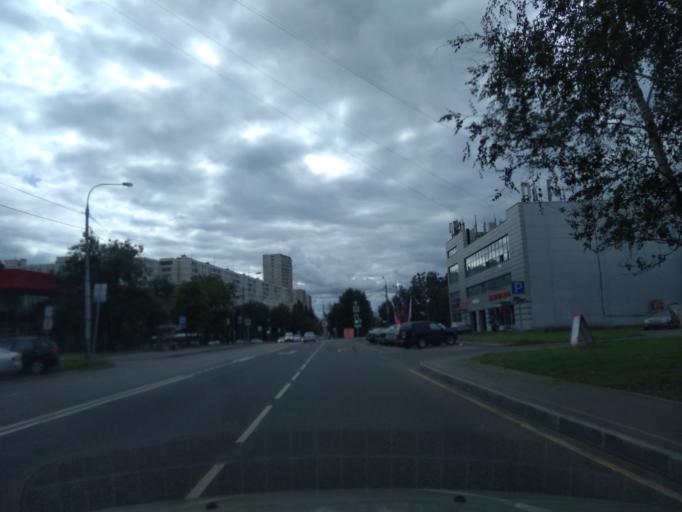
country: RU
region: Moscow
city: Strogino
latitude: 55.8146
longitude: 37.3930
